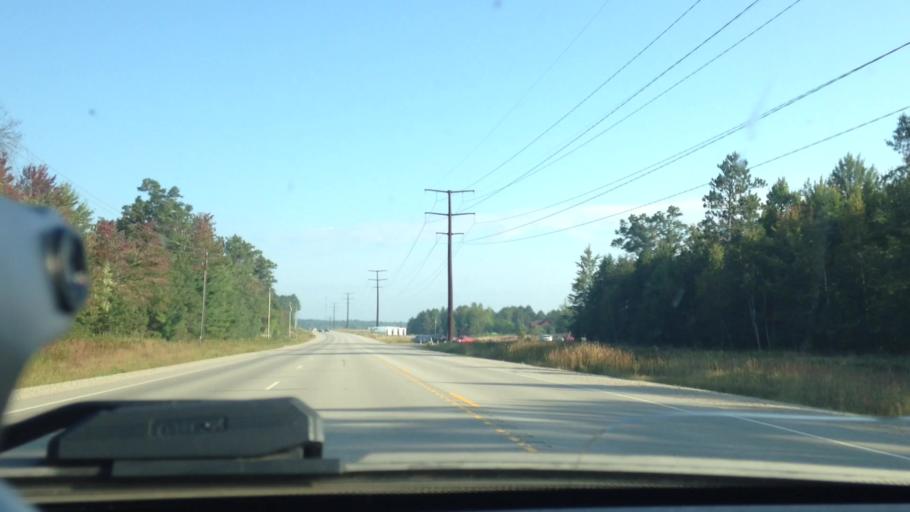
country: US
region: Wisconsin
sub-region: Marinette County
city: Peshtigo
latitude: 45.1944
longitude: -87.9947
